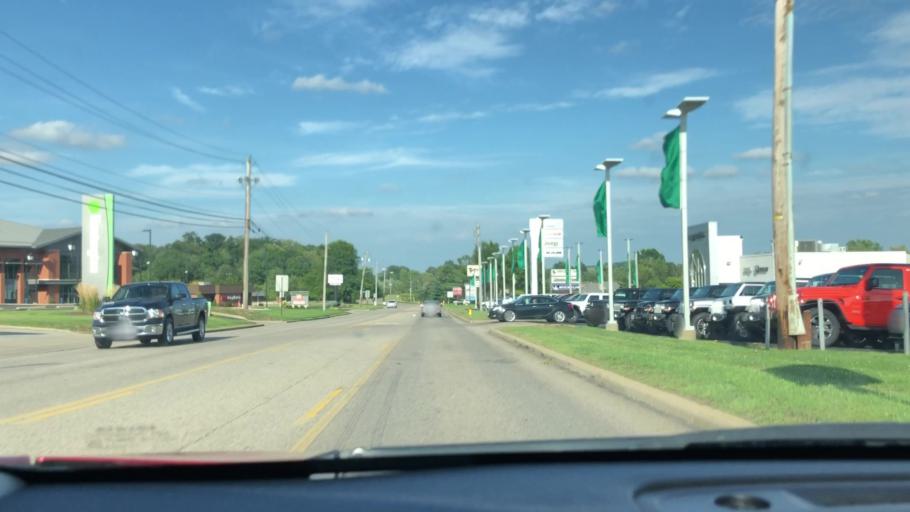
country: US
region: Ohio
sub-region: Stark County
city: Massillon
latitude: 40.8203
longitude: -81.5017
